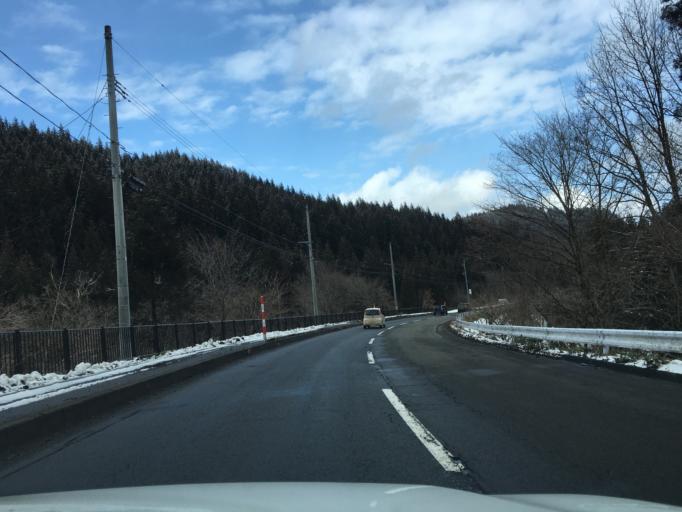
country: JP
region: Akita
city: Takanosu
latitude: 39.9904
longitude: 140.2462
